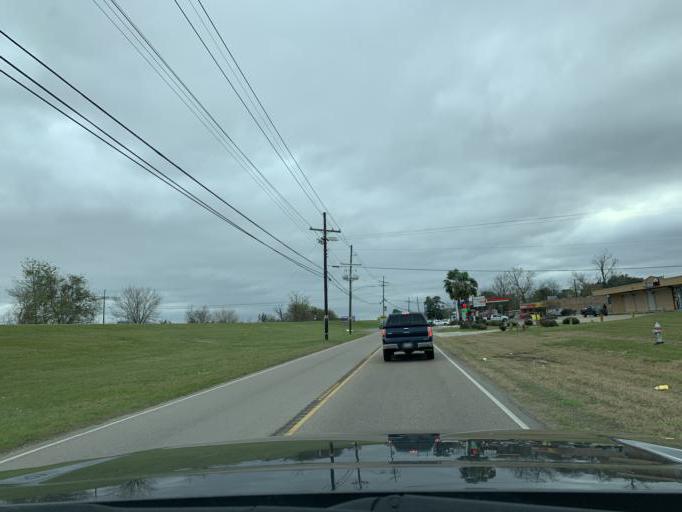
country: US
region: Louisiana
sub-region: Jefferson Parish
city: River Ridge
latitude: 29.9503
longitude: -90.2325
